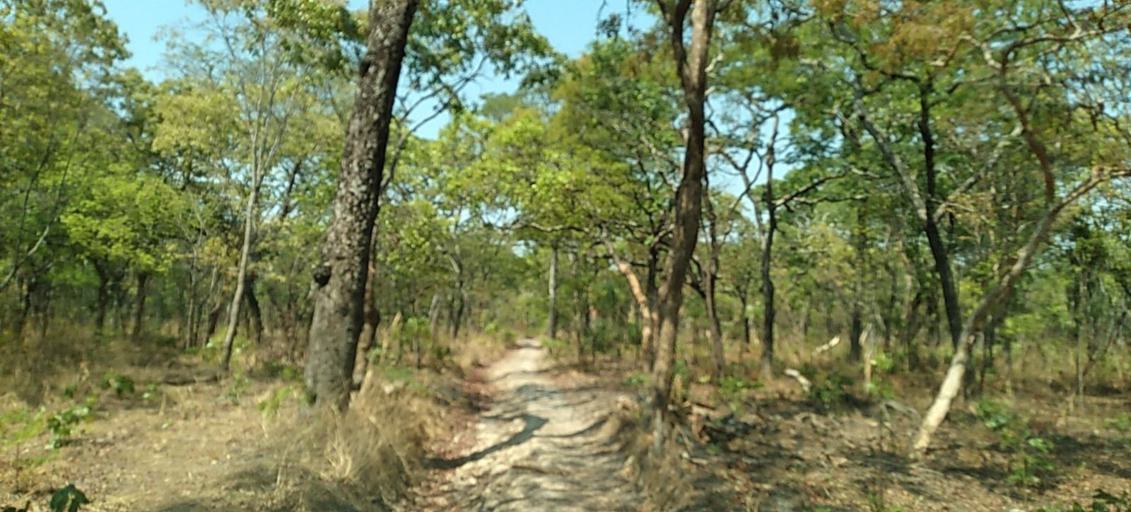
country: ZM
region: Copperbelt
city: Mpongwe
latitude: -13.7957
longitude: 28.0848
